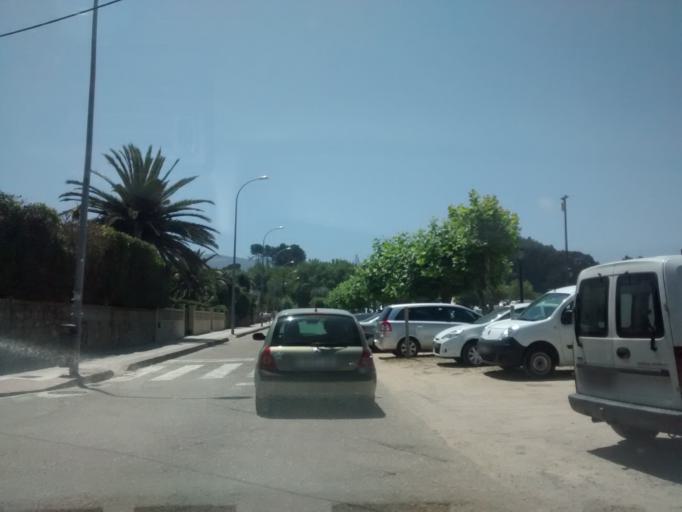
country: ES
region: Galicia
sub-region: Provincia de Pontevedra
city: Nigran
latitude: 42.1268
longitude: -8.8198
